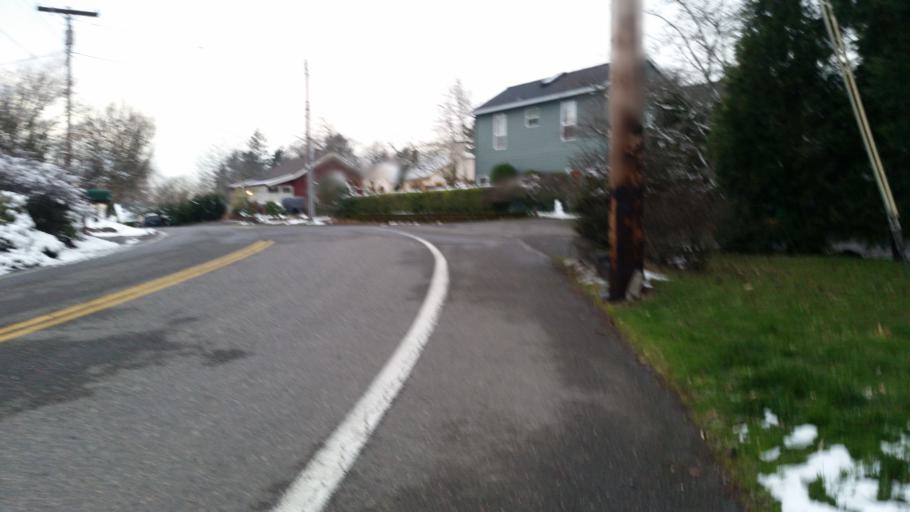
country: US
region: Oregon
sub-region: Washington County
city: Garden Home-Whitford
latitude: 45.4779
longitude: -122.7130
